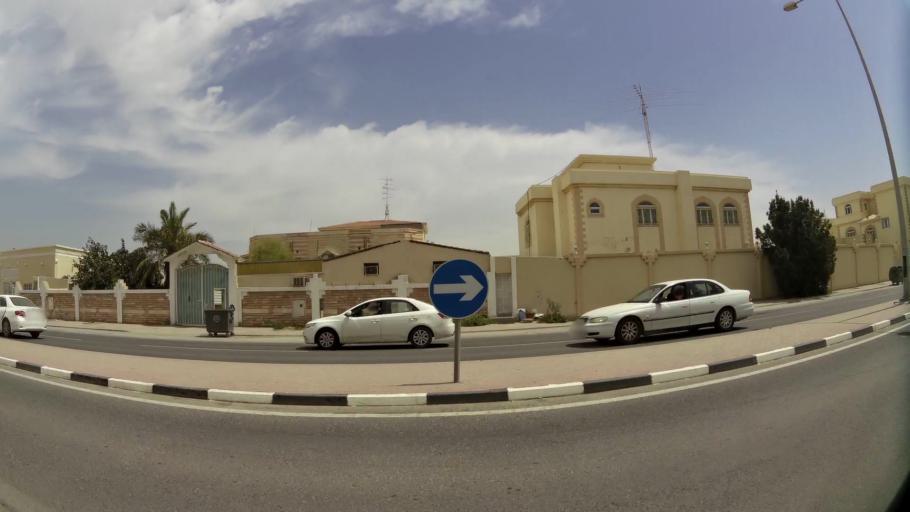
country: QA
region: Baladiyat ar Rayyan
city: Ar Rayyan
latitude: 25.2821
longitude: 51.4202
